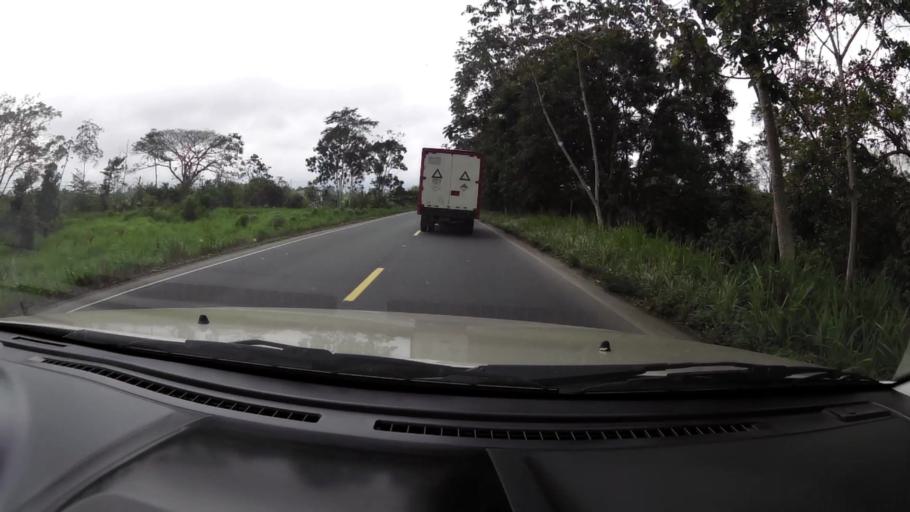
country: EC
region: Guayas
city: Balao
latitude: -2.8846
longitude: -79.7049
